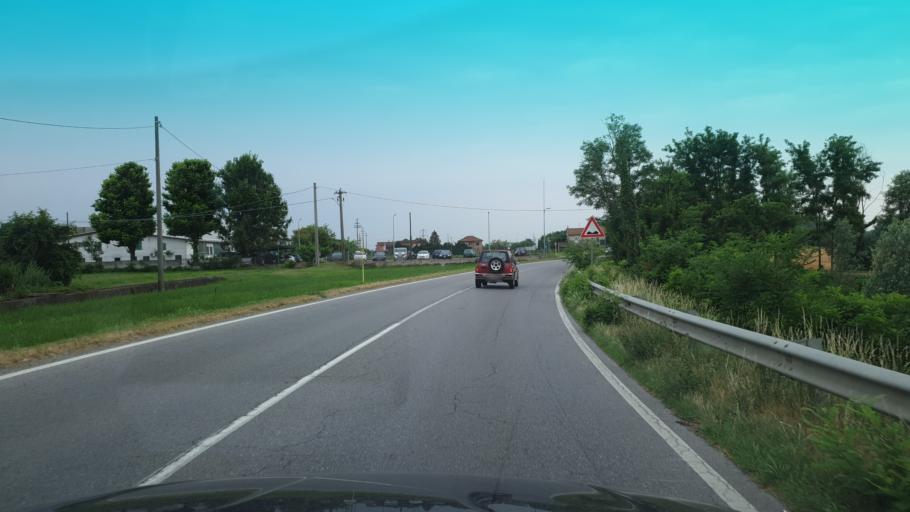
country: IT
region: Lombardy
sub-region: Provincia di Bergamo
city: Badalasco
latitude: 45.5290
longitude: 9.5380
